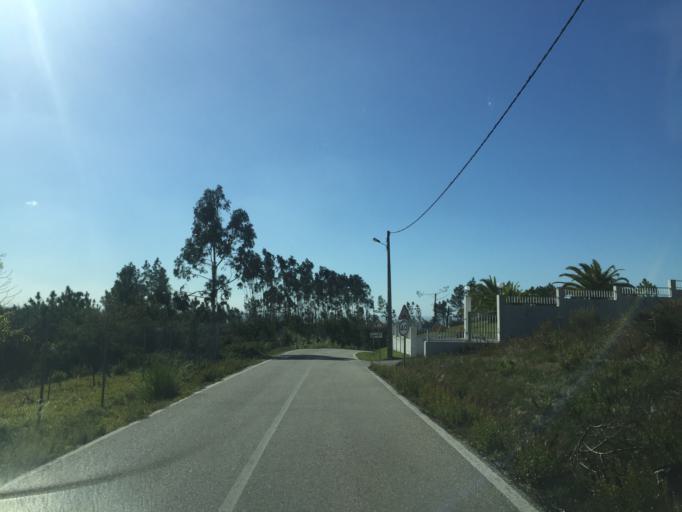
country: PT
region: Coimbra
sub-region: Figueira da Foz
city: Tavarede
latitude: 40.1877
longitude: -8.8359
